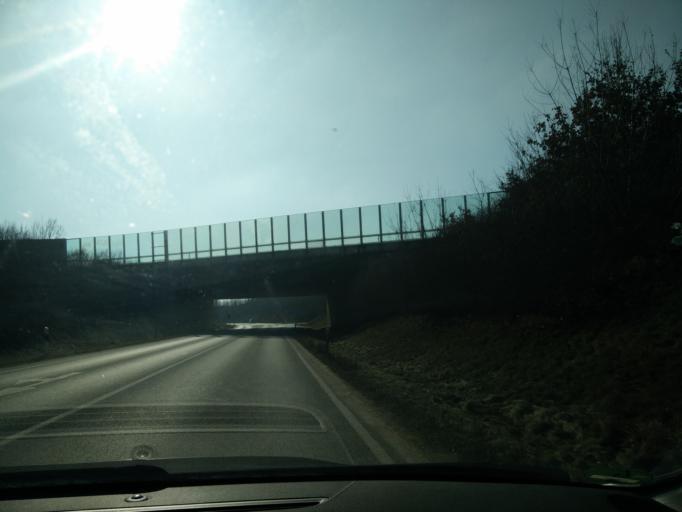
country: DE
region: Saxony
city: Muhlau
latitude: 50.8823
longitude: 12.7827
